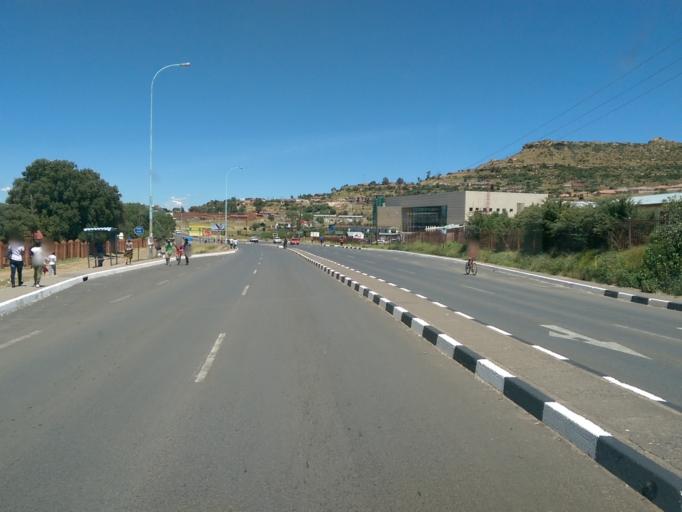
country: LS
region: Maseru
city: Maseru
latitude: -29.3209
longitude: 27.4973
